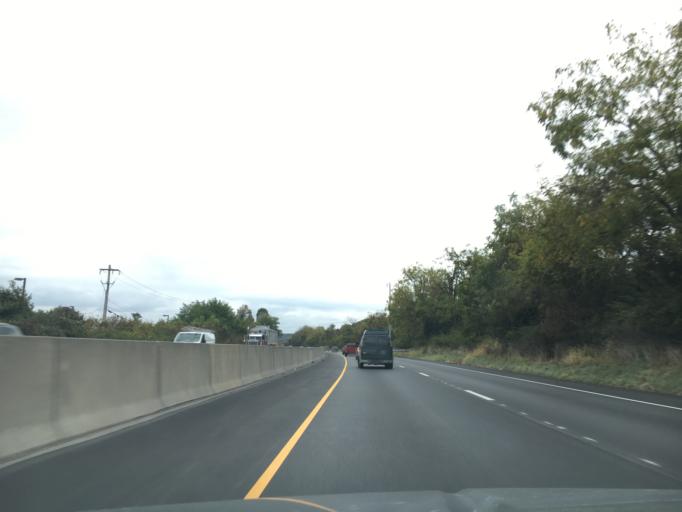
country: US
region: Pennsylvania
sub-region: Chester County
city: Downingtown
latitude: 40.0206
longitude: -75.6842
